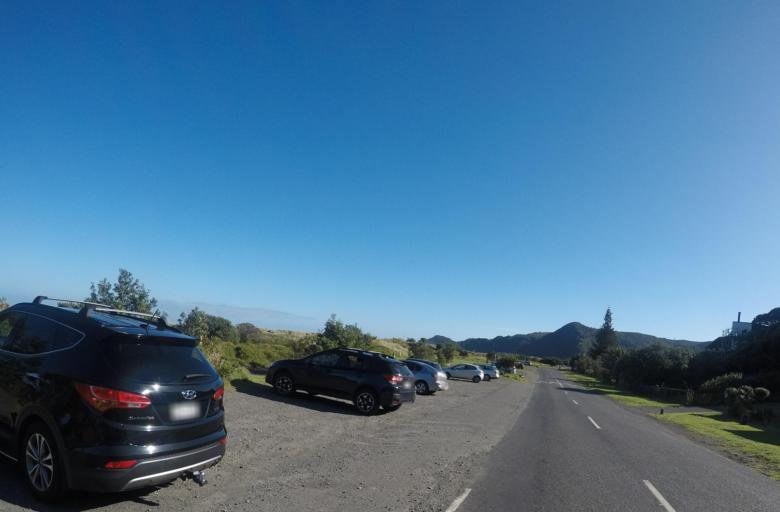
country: NZ
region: Auckland
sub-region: Auckland
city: Muriwai Beach
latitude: -36.9526
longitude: 174.4685
